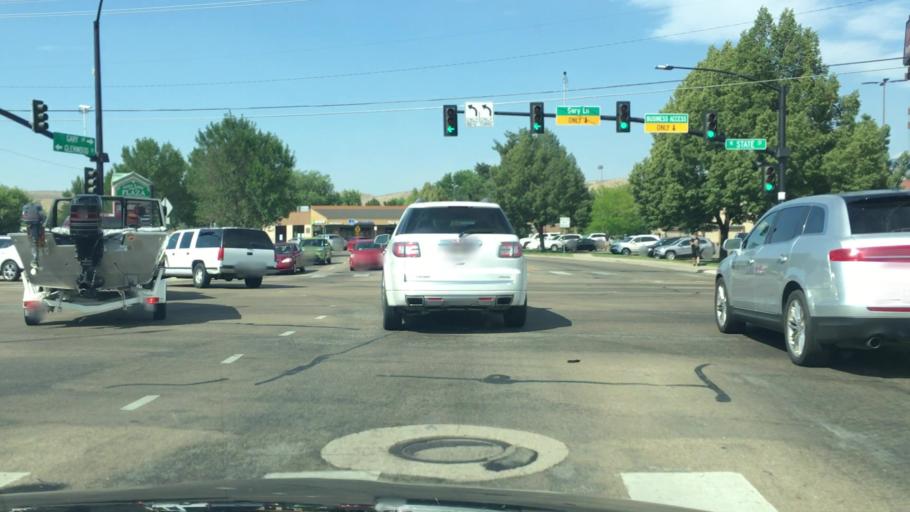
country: US
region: Idaho
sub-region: Ada County
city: Garden City
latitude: 43.6682
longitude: -116.2792
